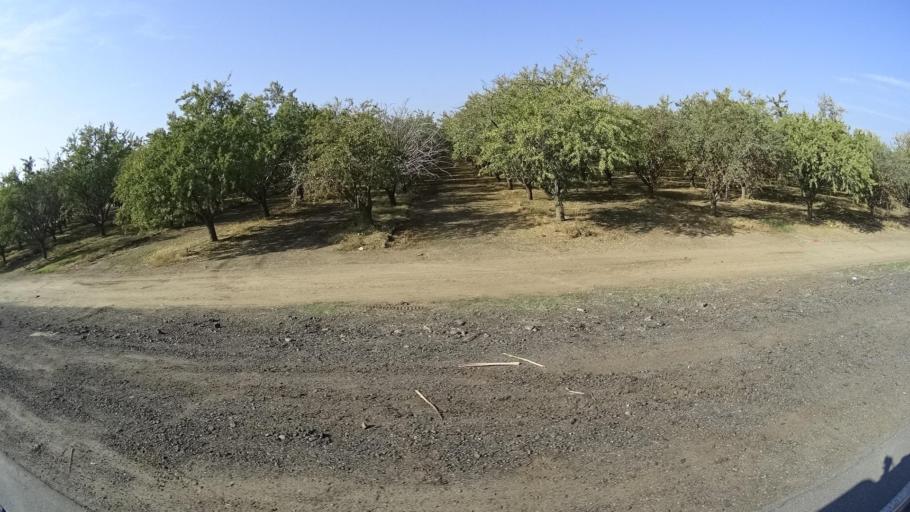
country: US
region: California
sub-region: Kern County
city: McFarland
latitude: 35.7188
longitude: -119.2231
